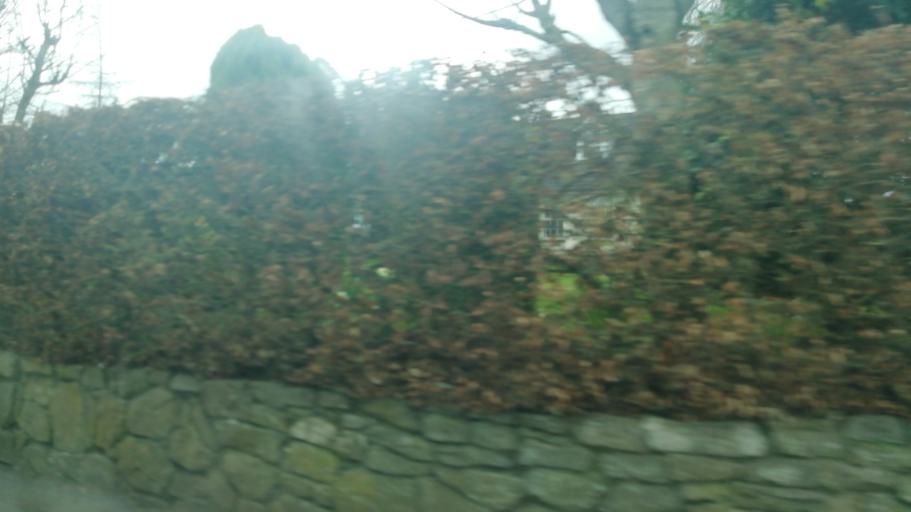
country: IE
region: Leinster
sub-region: Kildare
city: Rathangan
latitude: 53.2258
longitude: -6.9907
